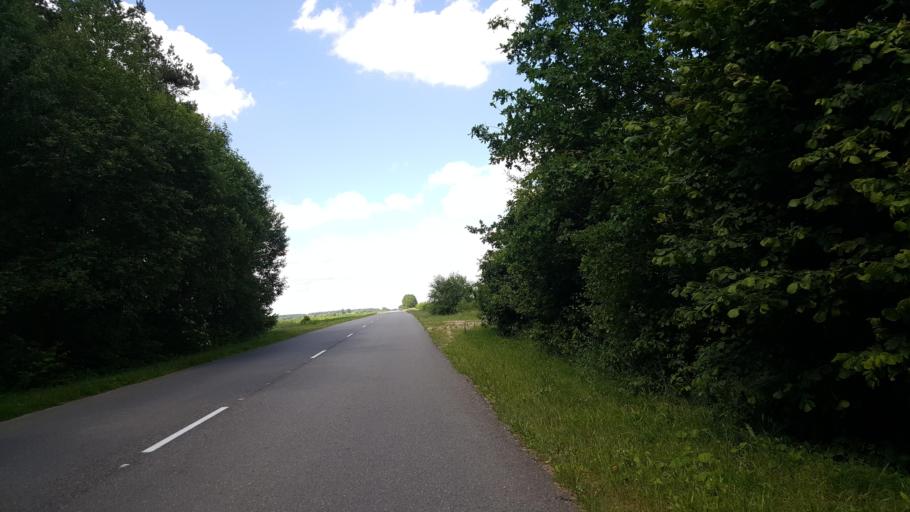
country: BY
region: Brest
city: Kamyanyets
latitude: 52.3764
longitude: 23.6171
